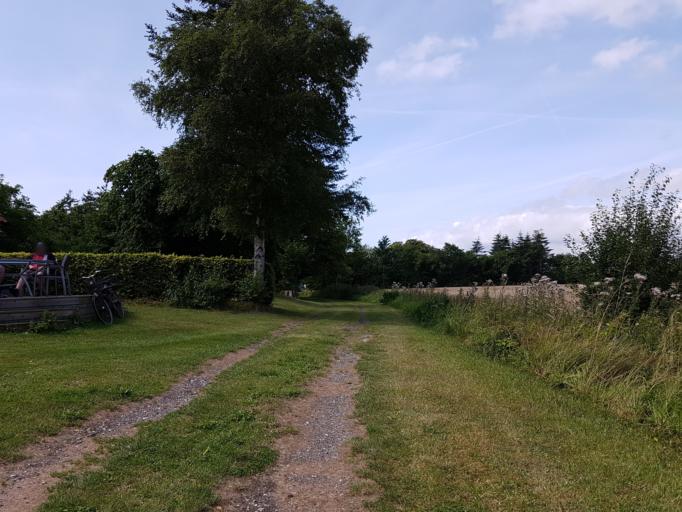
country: DK
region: Zealand
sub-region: Guldborgsund Kommune
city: Nykobing Falster
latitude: 54.6034
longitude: 11.9414
